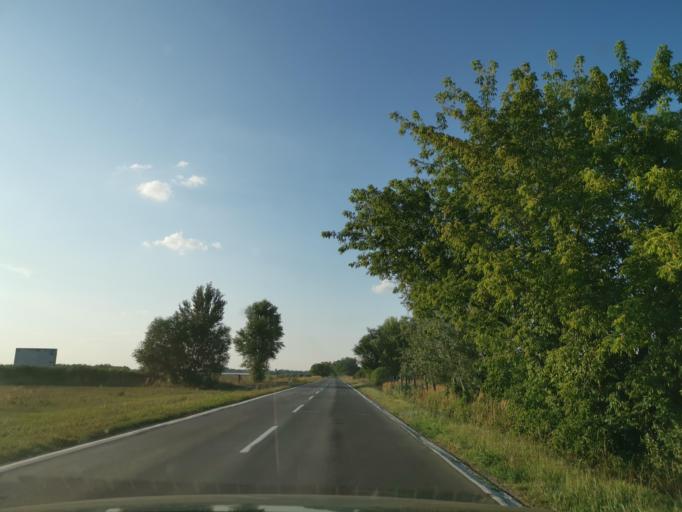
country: SK
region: Bratislavsky
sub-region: Okres Malacky
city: Malacky
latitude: 48.5113
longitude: 16.9955
